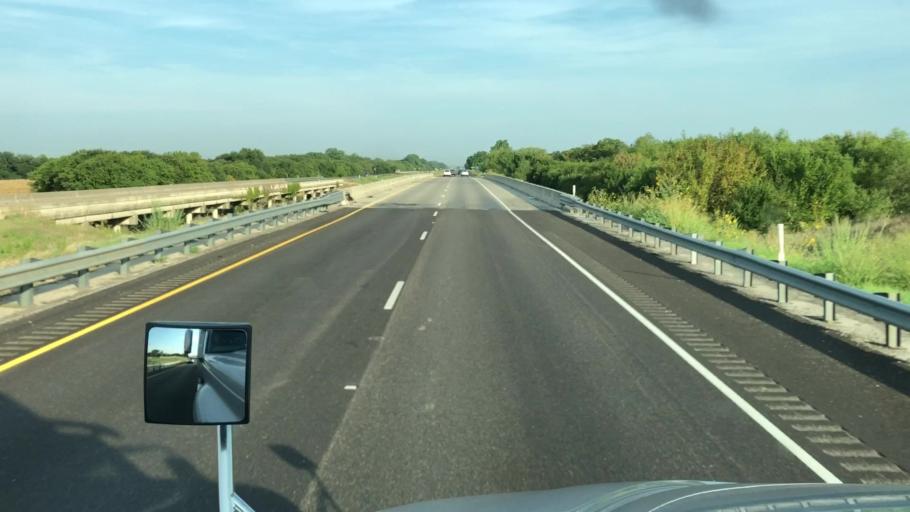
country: US
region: Texas
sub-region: McLennan County
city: Bellmead
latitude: 31.5345
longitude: -97.0266
